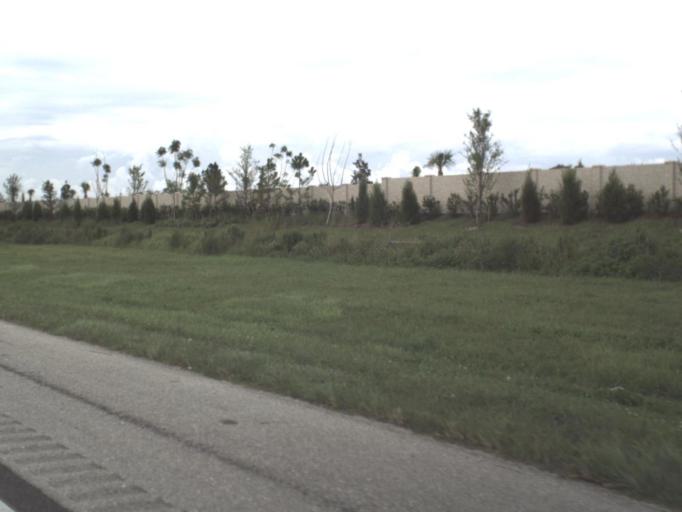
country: US
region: Florida
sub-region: Sarasota County
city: Lake Sarasota
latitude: 27.2575
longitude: -82.4494
